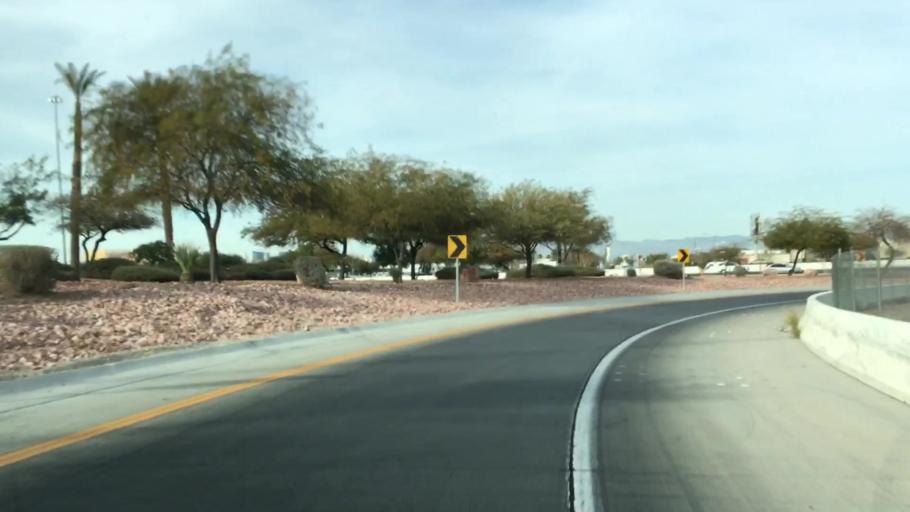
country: US
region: Nevada
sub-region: Clark County
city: Paradise
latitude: 36.0623
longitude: -115.1547
